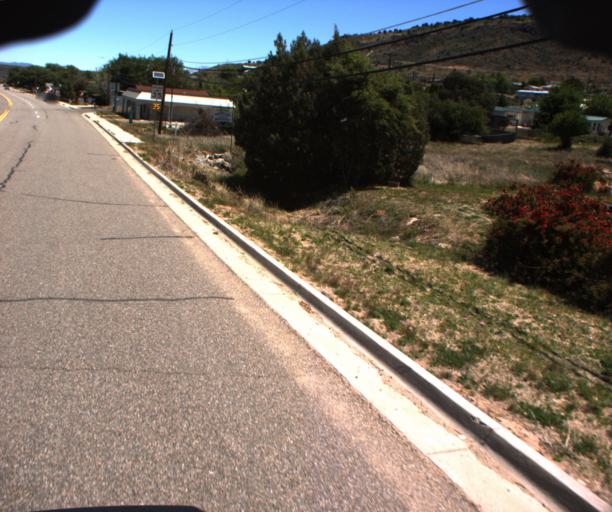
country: US
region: Arizona
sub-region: Yavapai County
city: Congress
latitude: 34.2183
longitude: -112.7498
